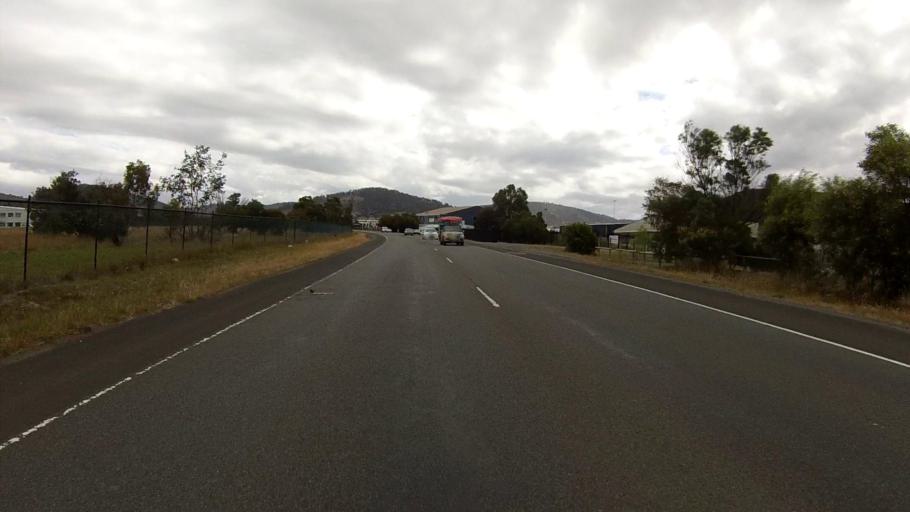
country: AU
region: Tasmania
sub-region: Clarence
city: Cambridge
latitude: -42.8301
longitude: 147.4752
